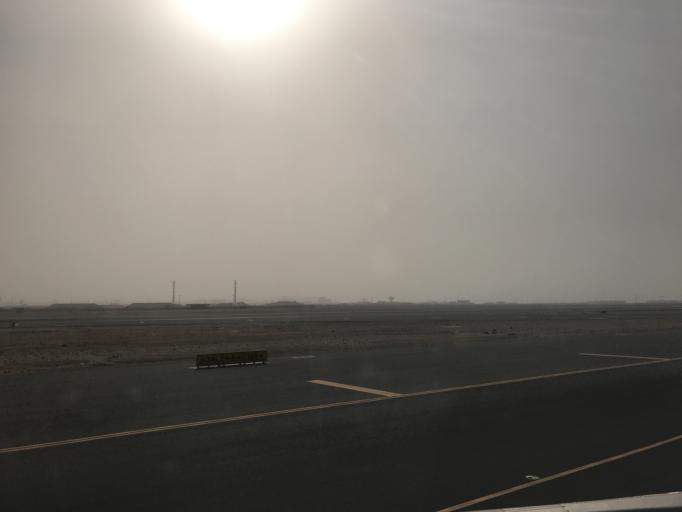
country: QA
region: Baladiyat ad Dawhah
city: Doha
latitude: 25.2794
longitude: 51.5970
